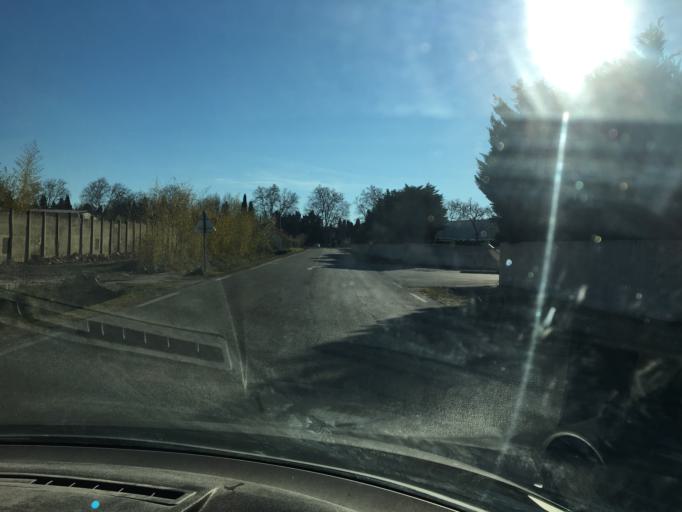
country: FR
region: Provence-Alpes-Cote d'Azur
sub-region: Departement des Bouches-du-Rhone
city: Maillane
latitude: 43.7977
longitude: 4.7888
